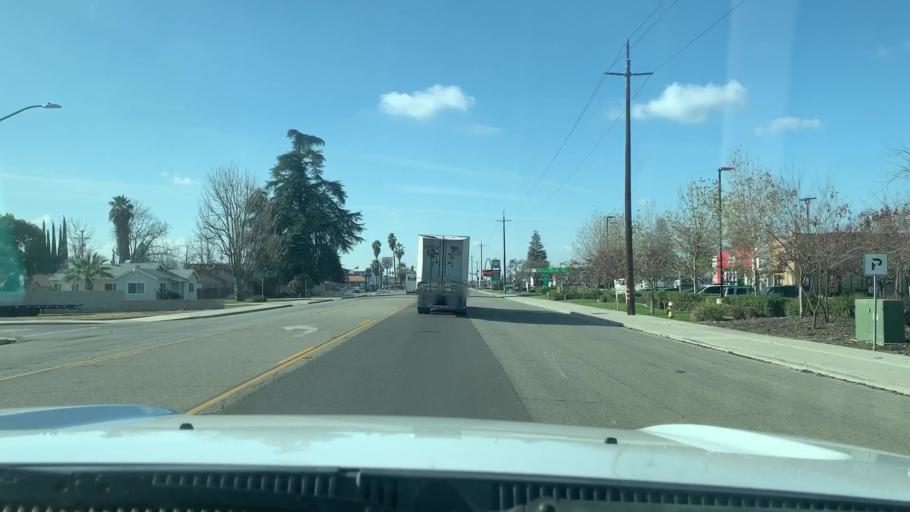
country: US
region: California
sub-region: Kern County
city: Wasco
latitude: 35.6016
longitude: -119.3467
